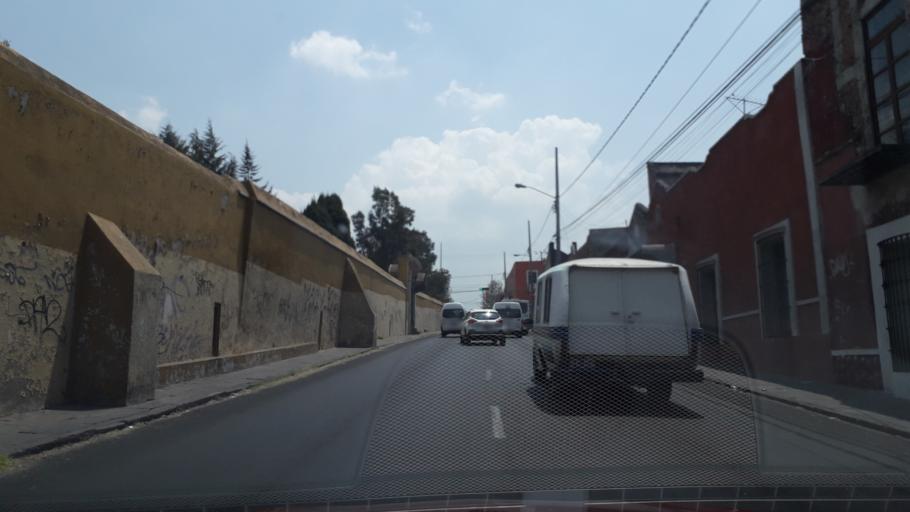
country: MX
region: Puebla
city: Puebla
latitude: 19.0477
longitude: -98.1873
